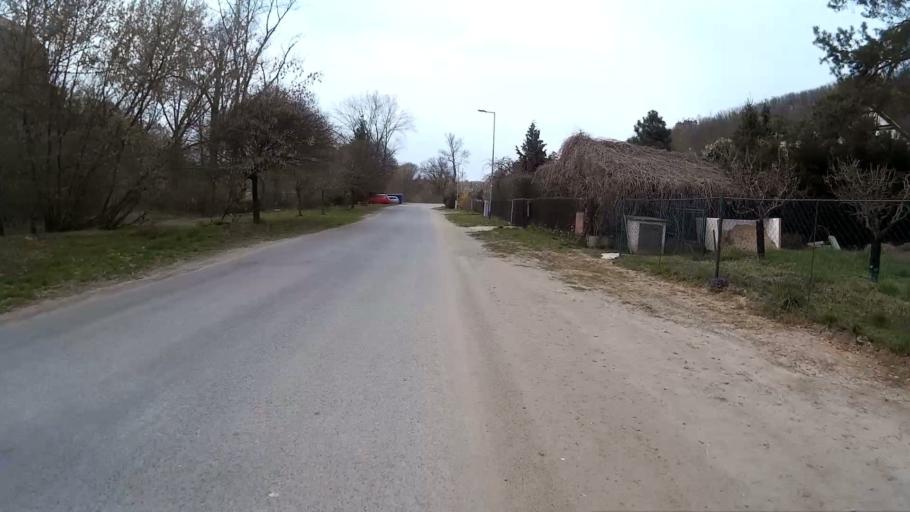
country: CZ
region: South Moravian
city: Dolni Kounice
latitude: 49.0677
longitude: 16.4751
